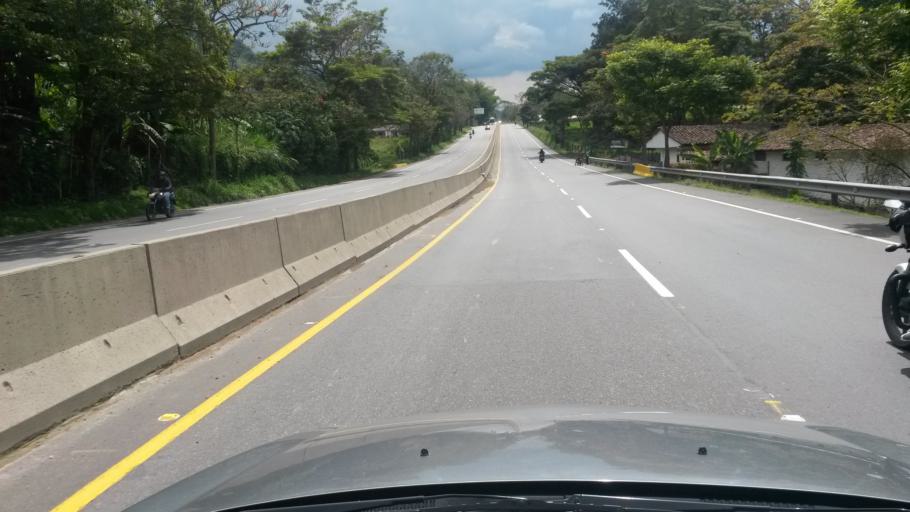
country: CO
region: Caldas
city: Palestina
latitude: 5.0109
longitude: -75.5943
